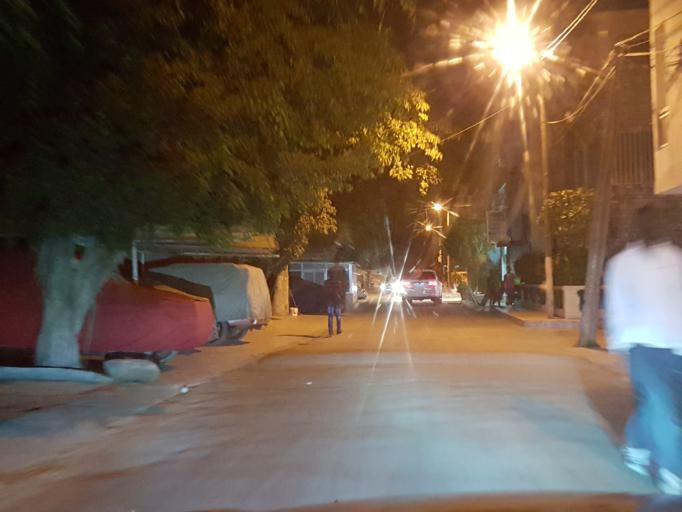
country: SN
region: Dakar
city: Grand Dakar
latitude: 14.7337
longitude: -17.4625
